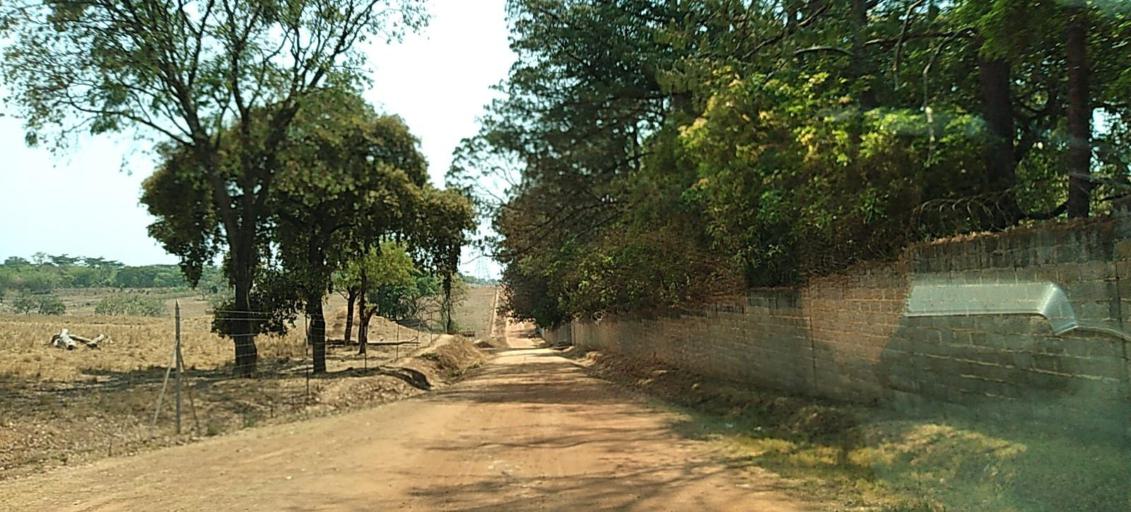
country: ZM
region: Copperbelt
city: Chambishi
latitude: -12.6234
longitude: 27.9430
